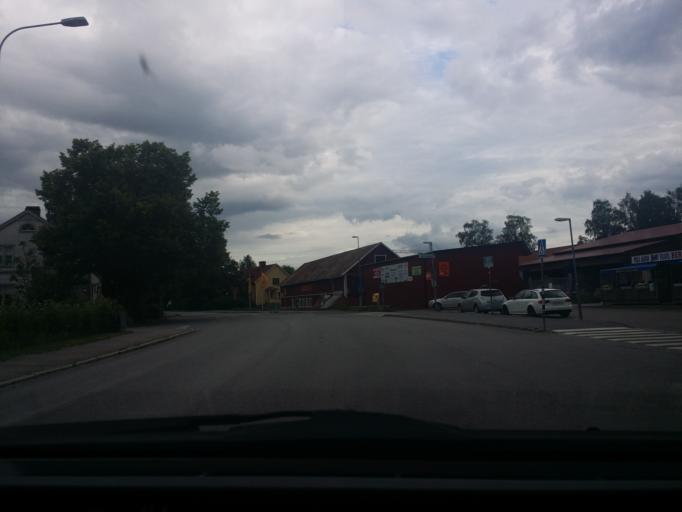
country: SE
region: OErebro
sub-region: Nora Kommun
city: Nora
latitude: 59.5244
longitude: 15.0350
